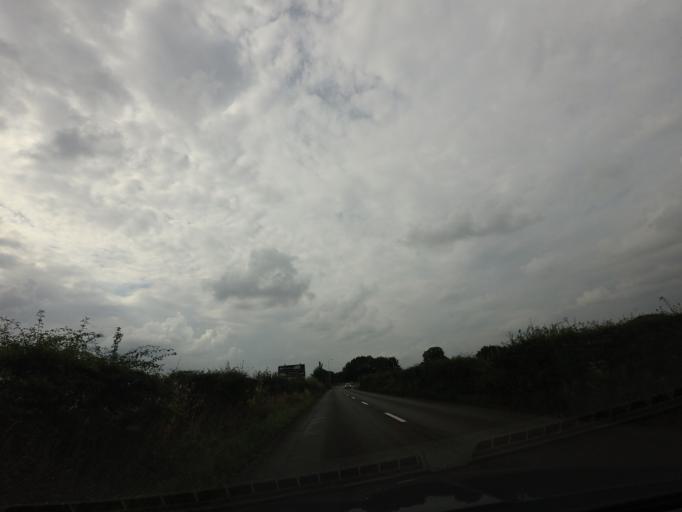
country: GB
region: England
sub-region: Shropshire
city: Tong
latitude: 52.6939
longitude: -2.3185
